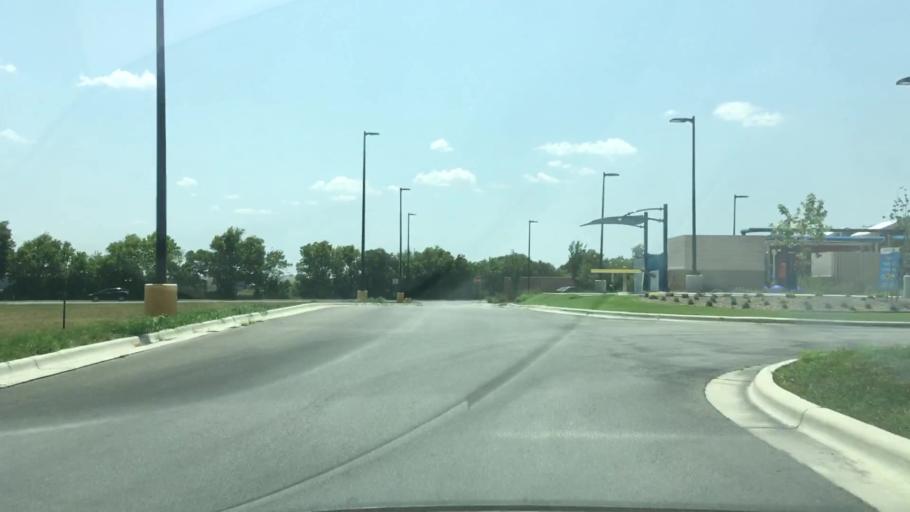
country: US
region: Texas
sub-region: Guadalupe County
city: Cibolo
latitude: 29.5725
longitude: -98.2384
